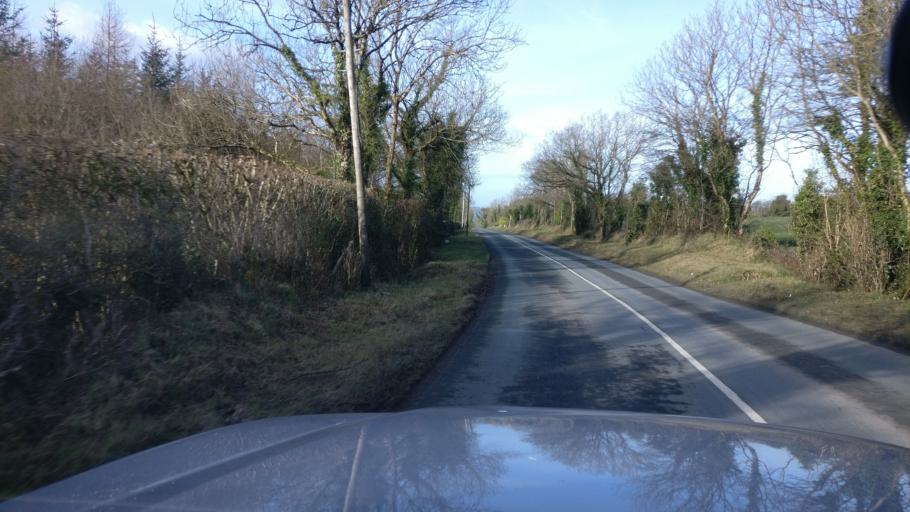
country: IE
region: Leinster
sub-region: Laois
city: Stradbally
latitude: 52.9363
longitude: -7.1962
